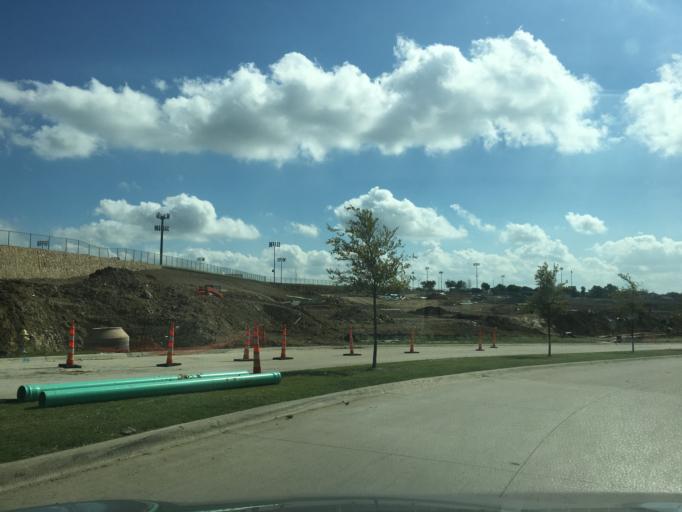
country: US
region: Texas
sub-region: Dallas County
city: Sachse
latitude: 32.9611
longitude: -96.5913
